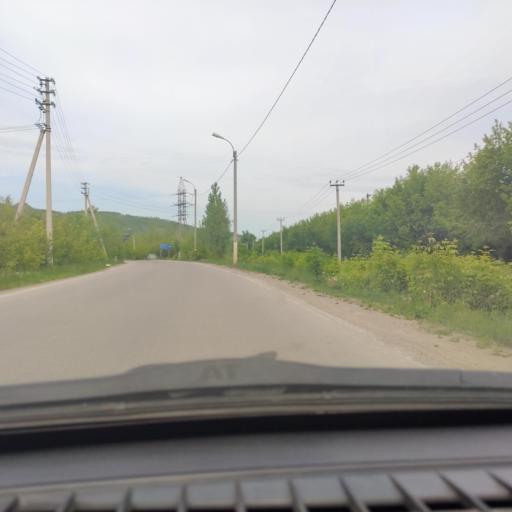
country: RU
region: Samara
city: Zhigulevsk
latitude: 53.4108
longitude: 49.4846
